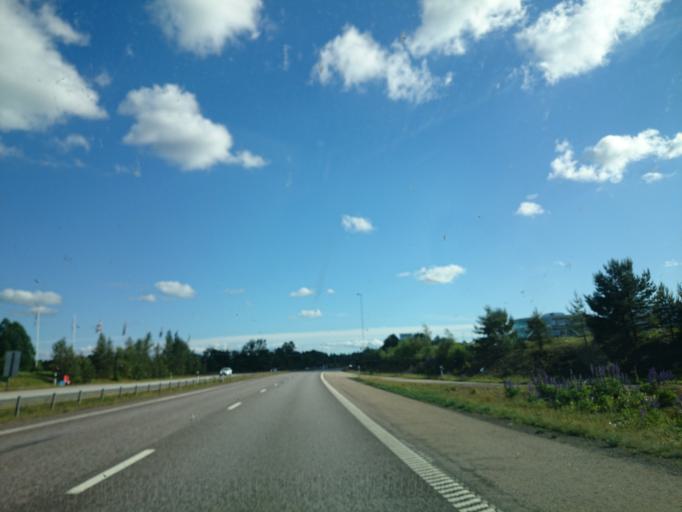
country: SE
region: Kronoberg
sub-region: Markaryds Kommun
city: Stromsnasbruk
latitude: 56.5605
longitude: 13.7204
